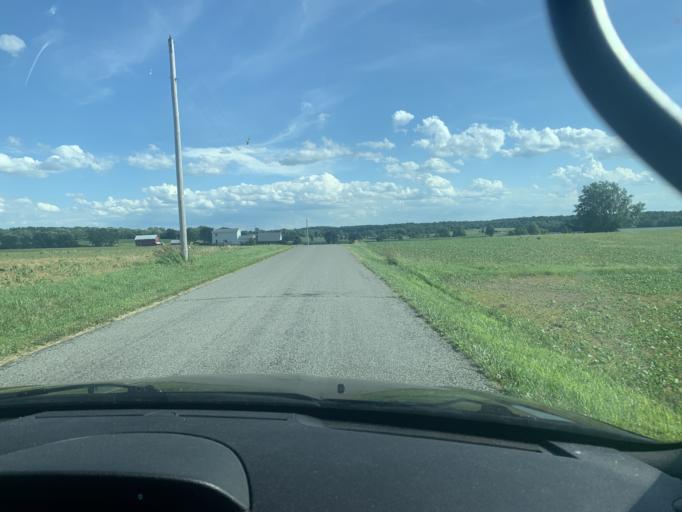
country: US
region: Ohio
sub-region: Logan County
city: De Graff
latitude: 40.2831
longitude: -83.8773
